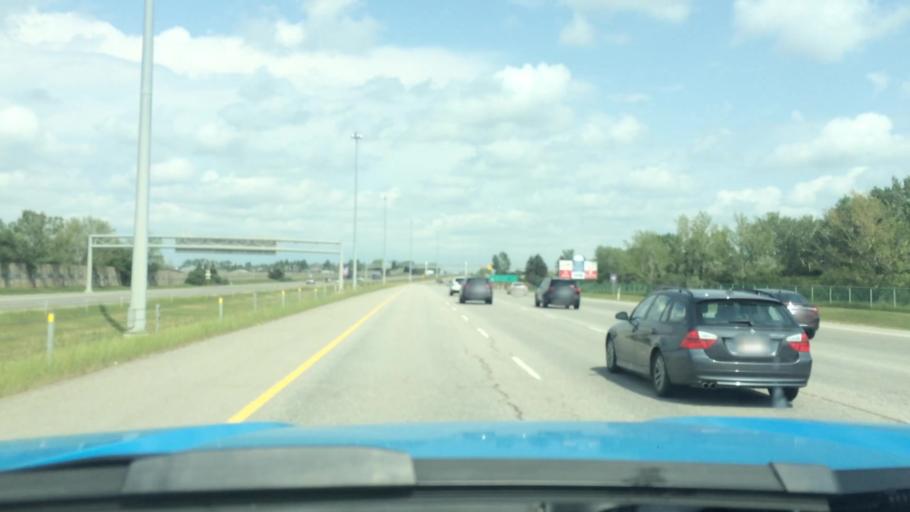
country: CA
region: Alberta
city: Airdrie
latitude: 51.2759
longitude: -114.0015
